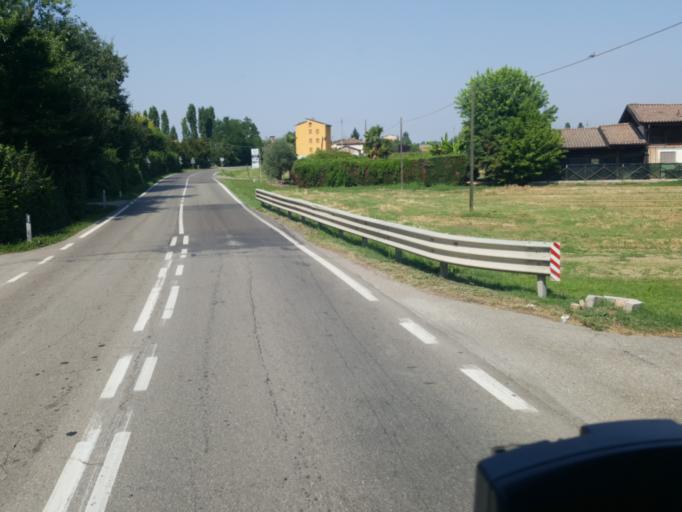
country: IT
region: Emilia-Romagna
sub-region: Provincia di Modena
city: Ca' di Sola
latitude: 44.5411
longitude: 10.9625
